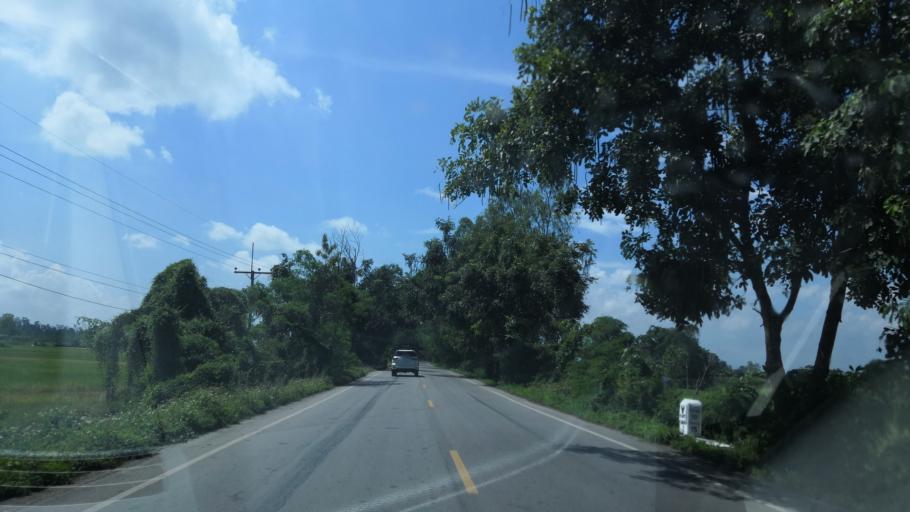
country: TH
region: Chiang Rai
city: Wiang Chai
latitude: 19.9628
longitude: 99.9588
